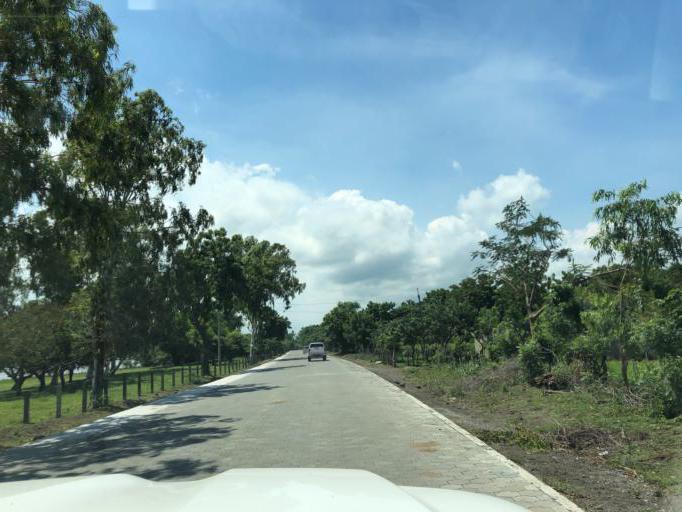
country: NI
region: Masaya
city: Tisma
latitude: 12.0615
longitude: -85.9095
